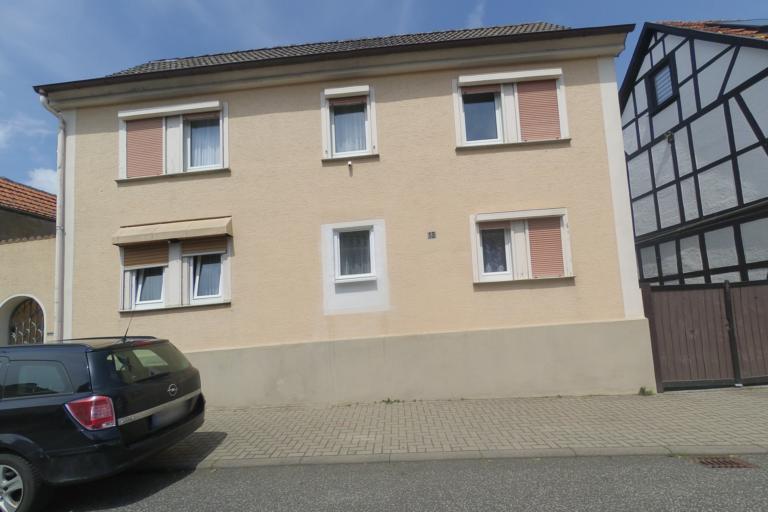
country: DE
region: Hesse
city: Nidderau
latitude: 50.2352
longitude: 8.8614
